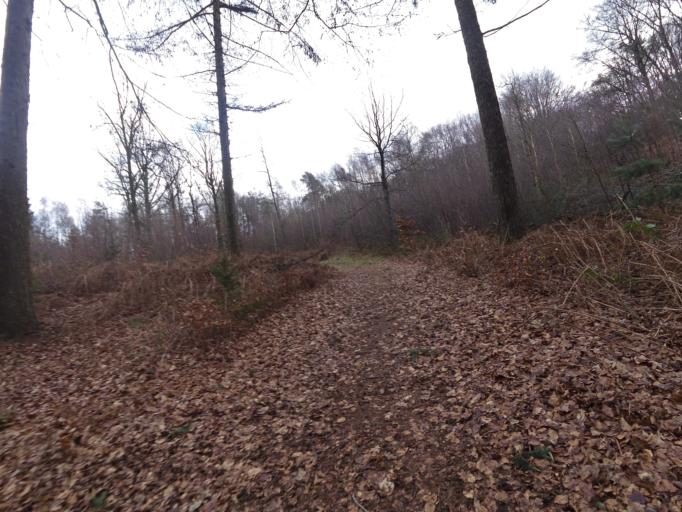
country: NL
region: Gelderland
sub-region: Gemeente Montferland
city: s-Heerenberg
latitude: 51.9223
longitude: 6.2369
